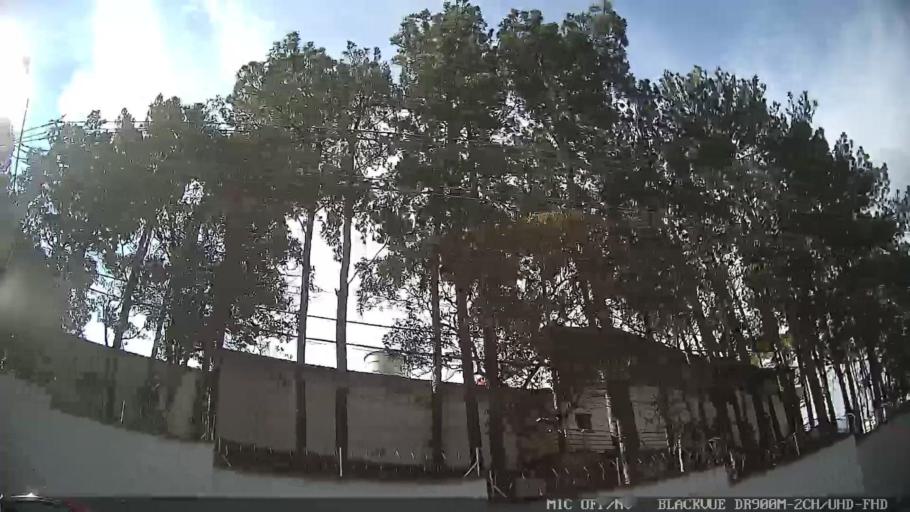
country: BR
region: Sao Paulo
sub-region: Braganca Paulista
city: Braganca Paulista
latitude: -22.9480
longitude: -46.5234
